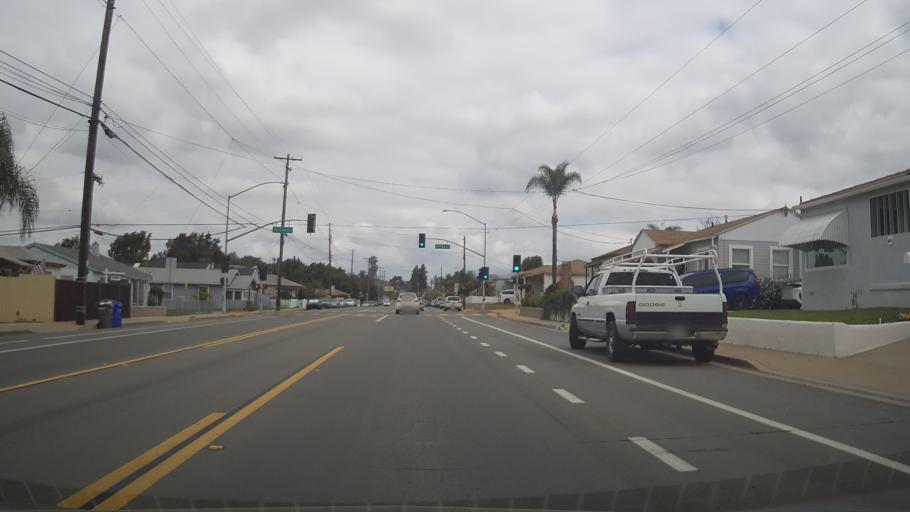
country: US
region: California
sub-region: San Diego County
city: La Mesa
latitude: 32.7627
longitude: -117.0468
